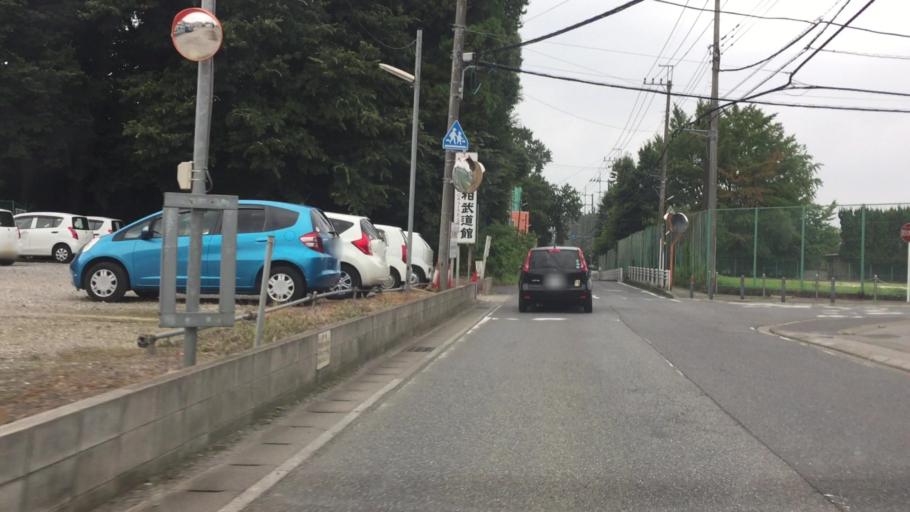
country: JP
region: Chiba
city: Kashiwa
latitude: 35.8082
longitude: 139.9656
